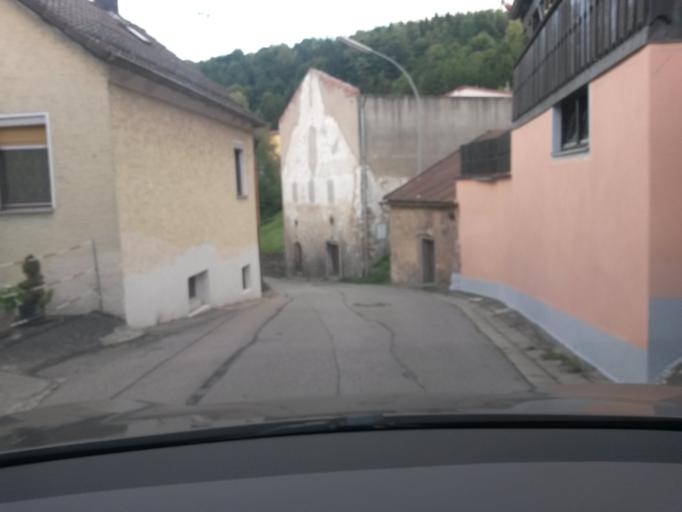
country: DE
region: Bavaria
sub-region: Upper Palatinate
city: Hohenfels
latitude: 49.2032
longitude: 11.8468
